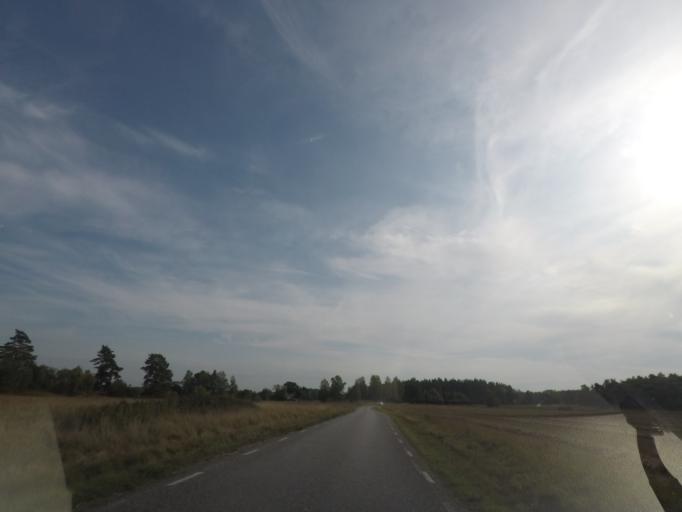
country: SE
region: Vaestmanland
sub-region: Kungsors Kommun
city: Kungsoer
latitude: 59.5238
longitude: 16.1455
